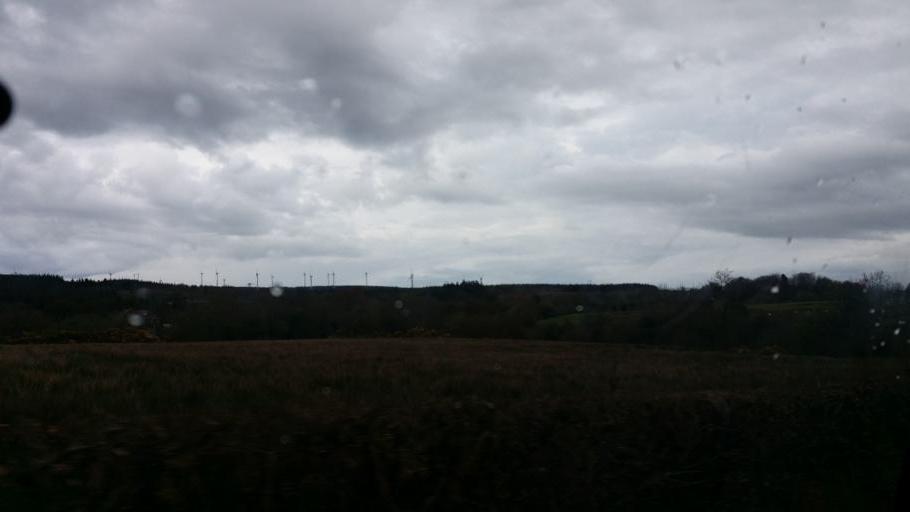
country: IE
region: Ulster
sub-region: An Cabhan
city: Ballyconnell
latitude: 54.1142
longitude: -7.6428
